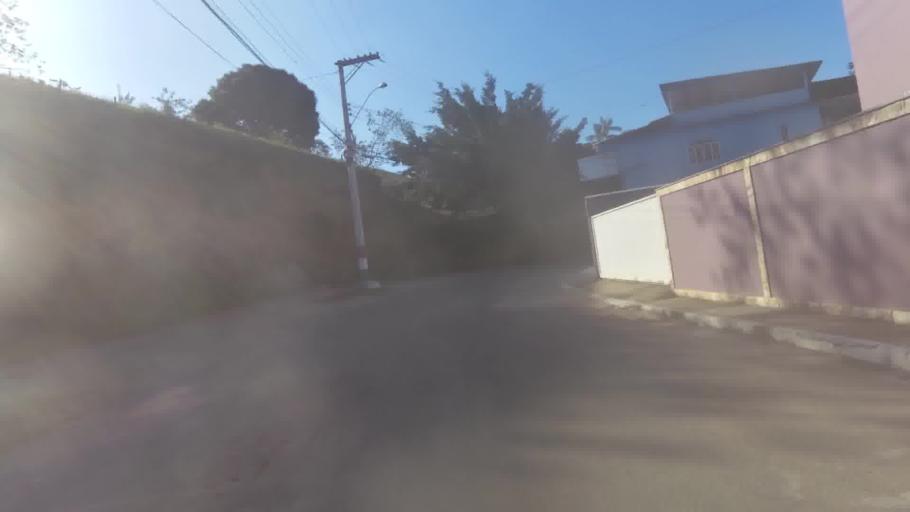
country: BR
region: Espirito Santo
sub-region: Iconha
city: Iconha
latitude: -20.7307
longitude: -40.7791
